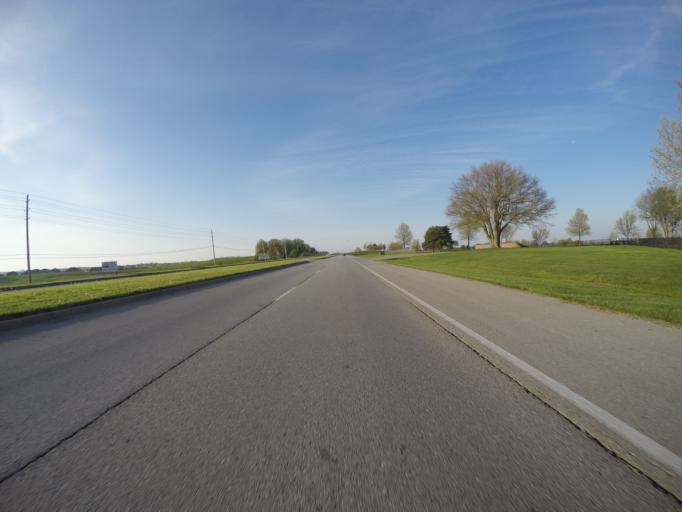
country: US
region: Missouri
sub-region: Jackson County
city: Lees Summit
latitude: 38.9188
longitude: -94.4507
